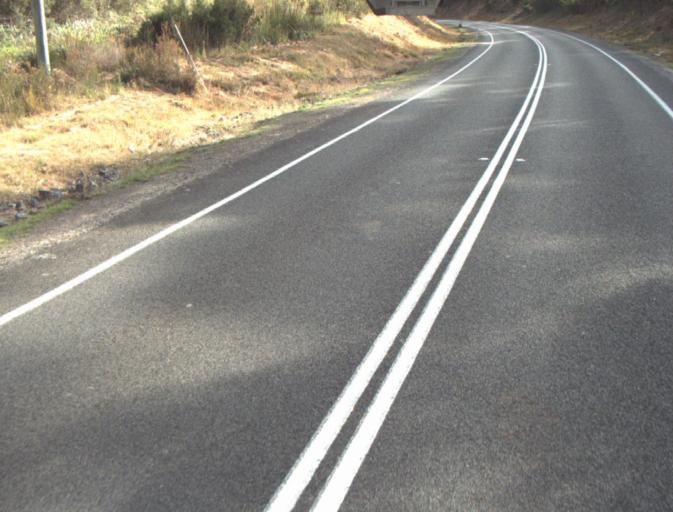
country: AU
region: Tasmania
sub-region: Launceston
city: Mayfield
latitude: -41.3092
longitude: 147.2028
